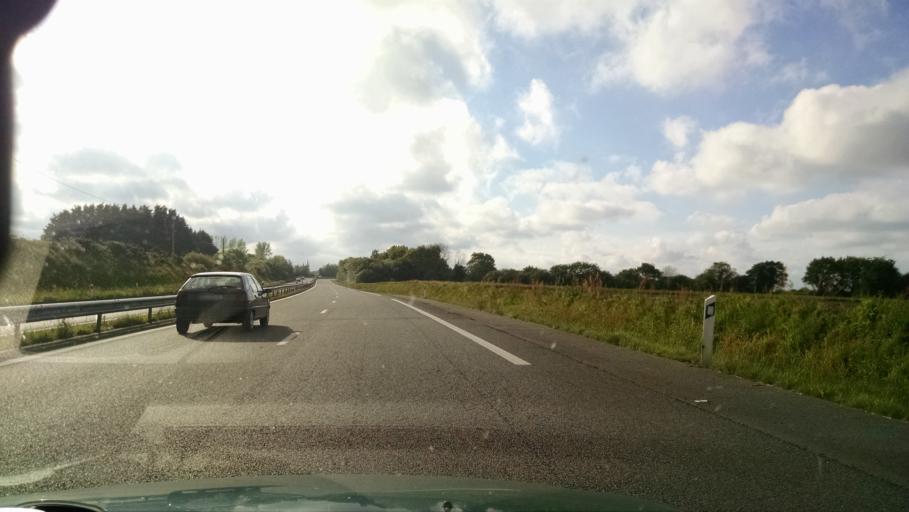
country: FR
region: Brittany
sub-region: Departement du Finistere
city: Henvic
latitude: 48.6278
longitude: -3.9124
